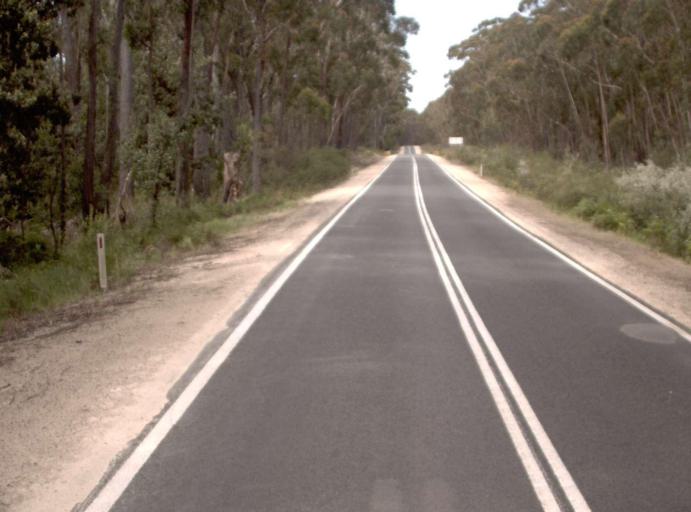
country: AU
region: New South Wales
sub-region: Bega Valley
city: Eden
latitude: -37.5014
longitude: 149.5381
